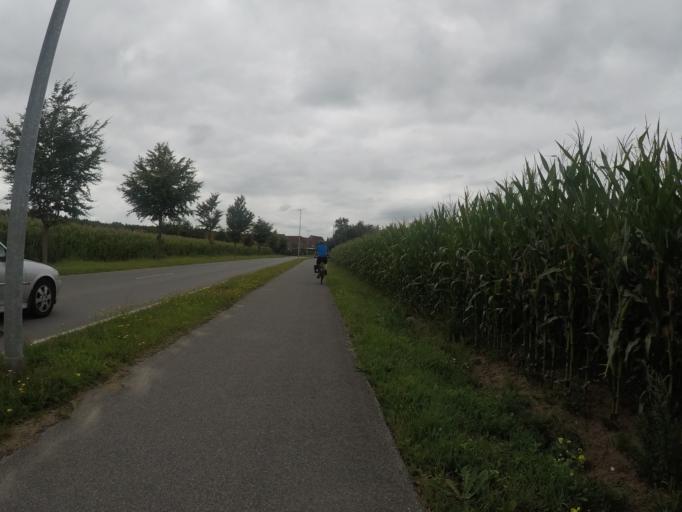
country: DE
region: Lower Saxony
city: Hammah
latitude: 53.5986
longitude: 9.4185
